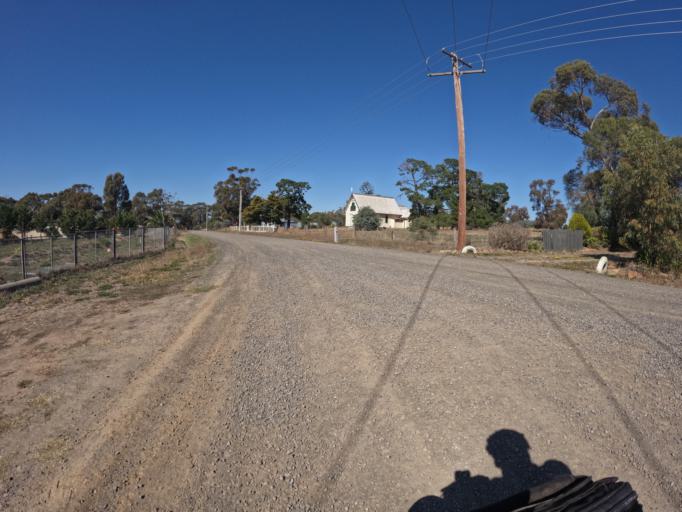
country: AU
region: Victoria
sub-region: Greater Bendigo
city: Kennington
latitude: -36.8271
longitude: 144.5850
